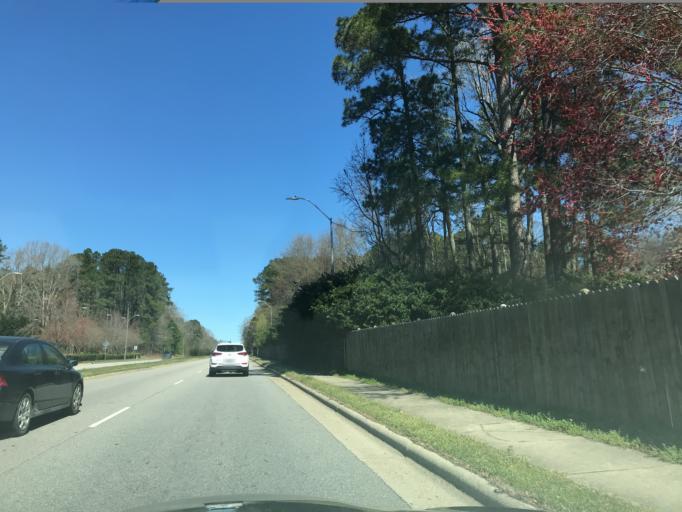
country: US
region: North Carolina
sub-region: Wake County
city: Garner
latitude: 35.7021
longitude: -78.6404
